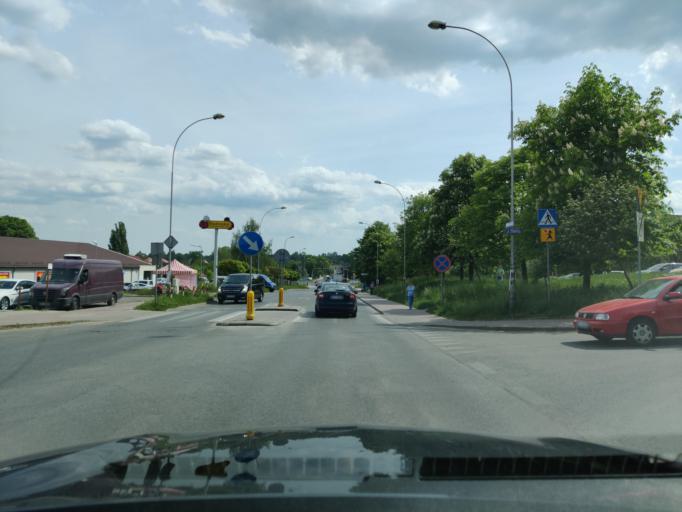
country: PL
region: Silesian Voivodeship
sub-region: Czestochowa
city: Czestochowa
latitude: 50.7725
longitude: 19.1504
